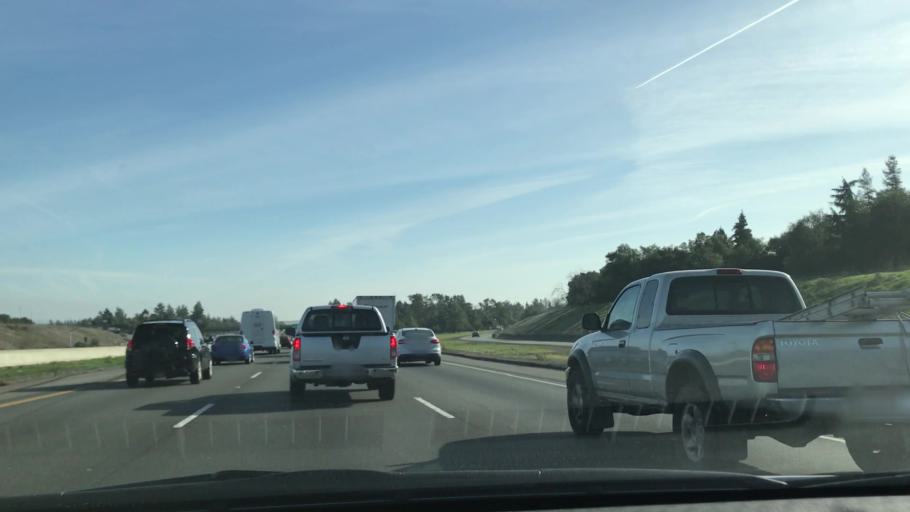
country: US
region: California
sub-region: Santa Clara County
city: Morgan Hill
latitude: 37.1565
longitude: -121.6563
